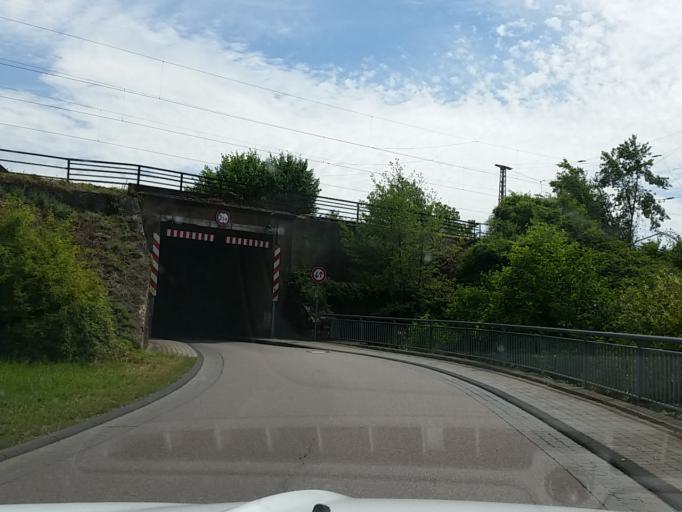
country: DE
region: Rheinland-Pfalz
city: Serrig
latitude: 49.5783
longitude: 6.5687
